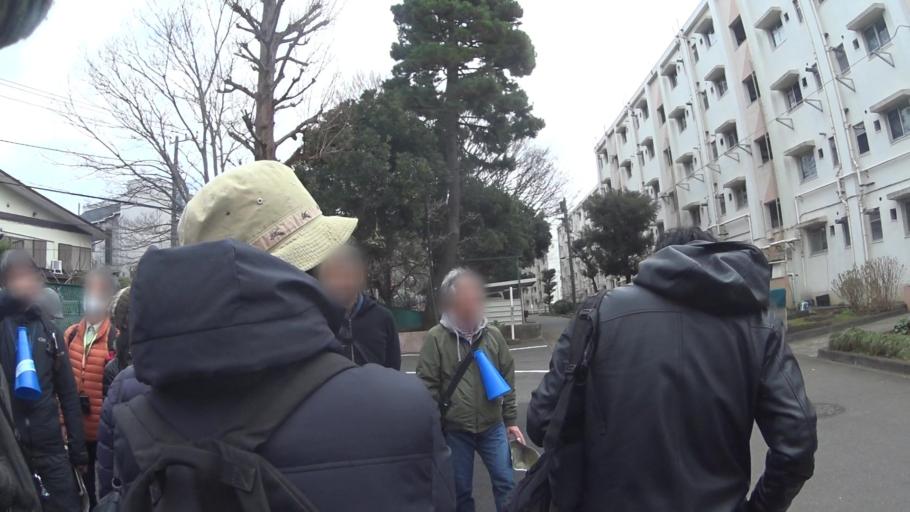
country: JP
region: Tokyo
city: Chofugaoka
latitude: 35.6342
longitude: 139.6076
